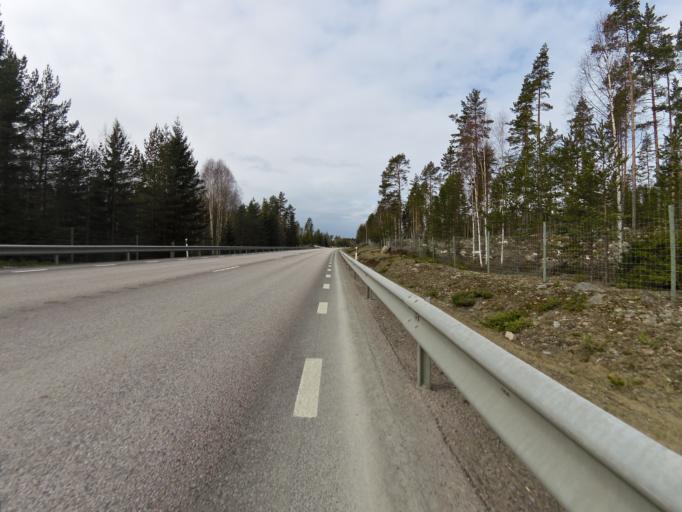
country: SE
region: Gaevleborg
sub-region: Hofors Kommun
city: Hofors
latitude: 60.5453
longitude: 16.1434
